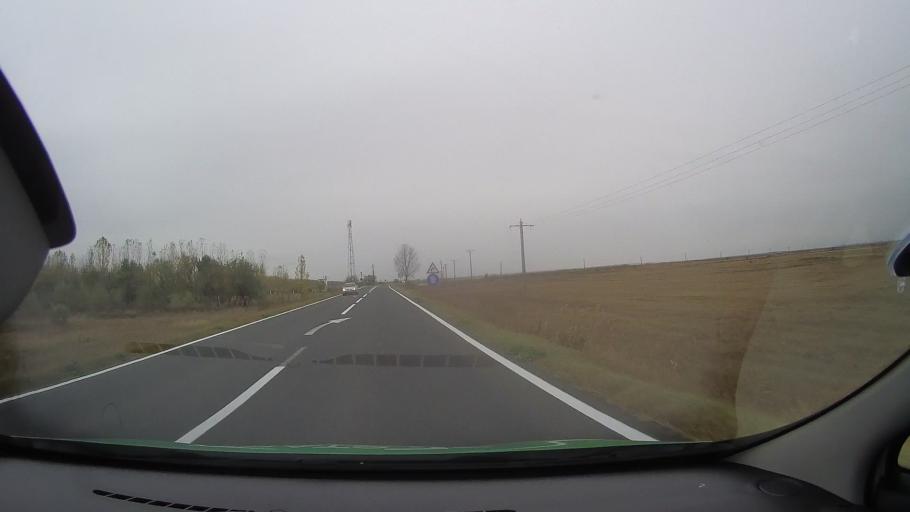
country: RO
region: Ialomita
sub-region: Comuna Giurgeni
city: Giurgeni
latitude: 44.7255
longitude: 27.8536
